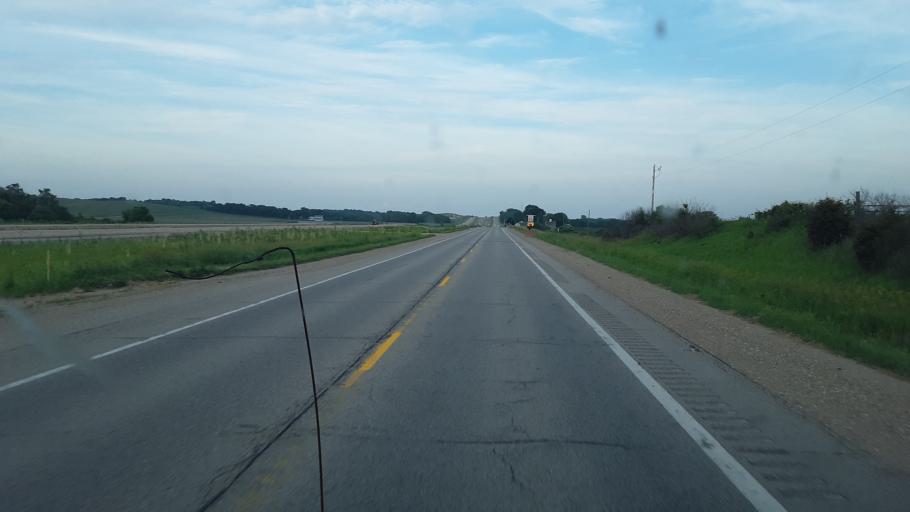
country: US
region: Iowa
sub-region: Tama County
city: Tama
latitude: 41.9638
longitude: -92.4756
